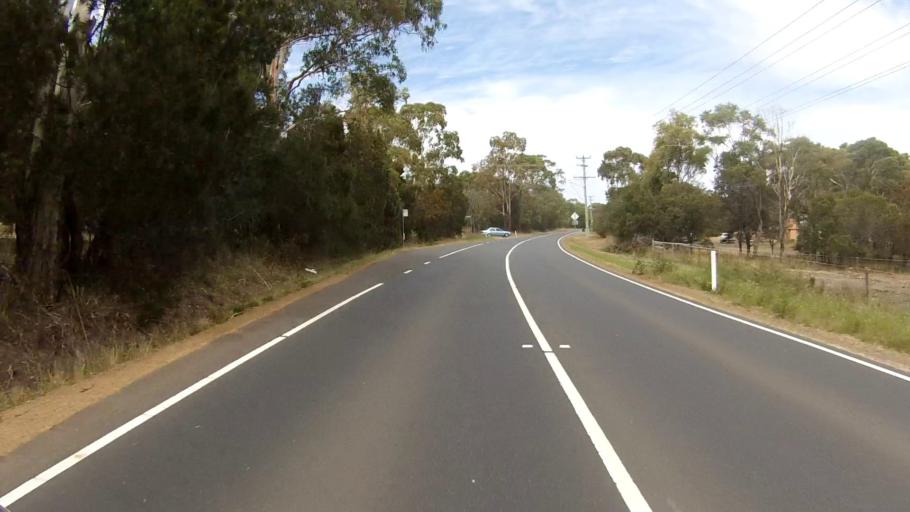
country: AU
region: Tasmania
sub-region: Clarence
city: Acton Park
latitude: -42.8743
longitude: 147.4829
